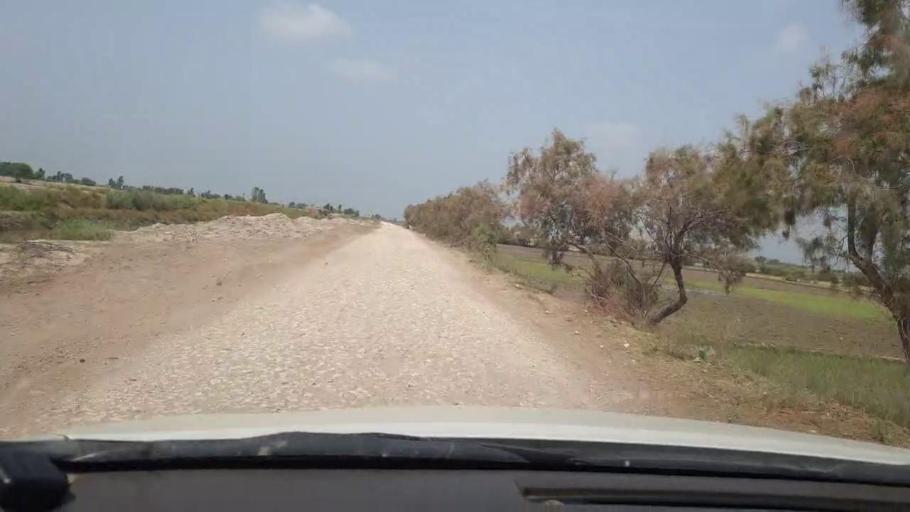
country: PK
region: Sindh
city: Garhi Yasin
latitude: 28.0129
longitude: 68.5303
